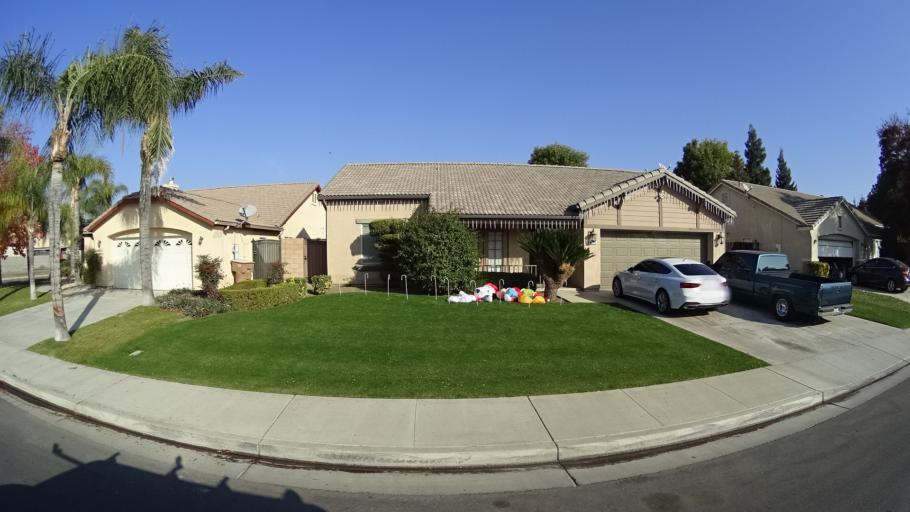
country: US
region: California
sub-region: Kern County
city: Greenacres
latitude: 35.3636
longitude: -119.1118
